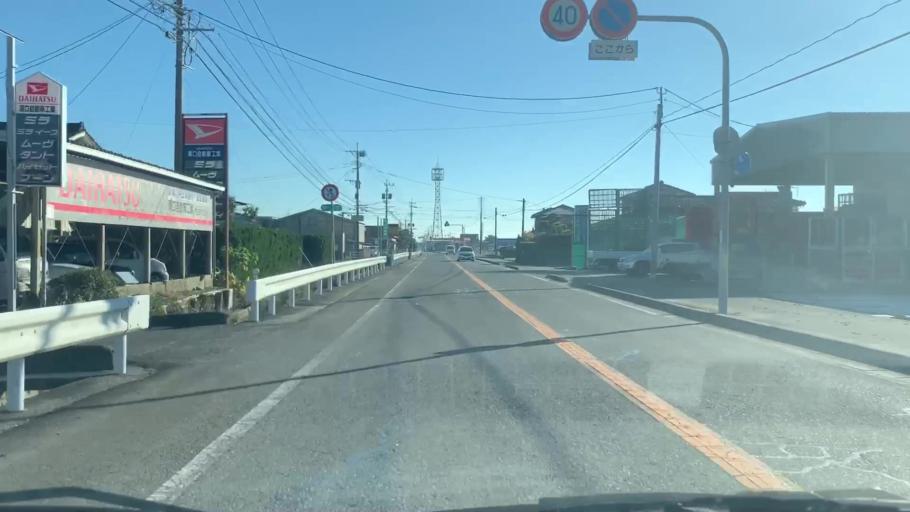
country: JP
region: Saga Prefecture
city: Kashima
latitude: 33.1828
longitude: 130.1782
